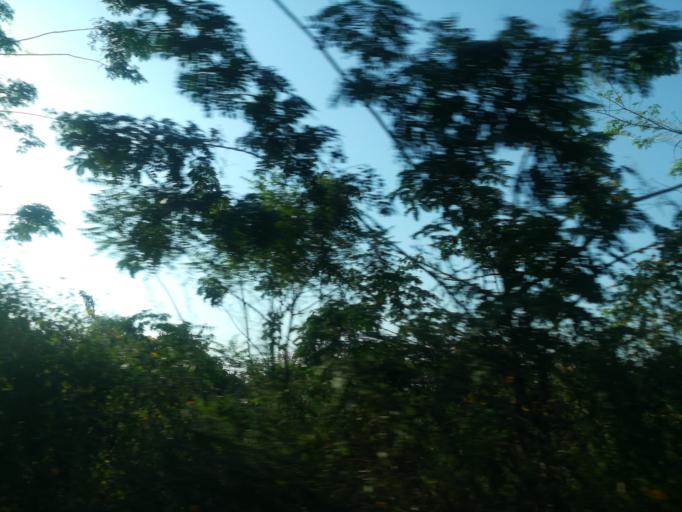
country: NG
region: Ogun
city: Abeokuta
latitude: 7.2037
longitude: 3.2898
